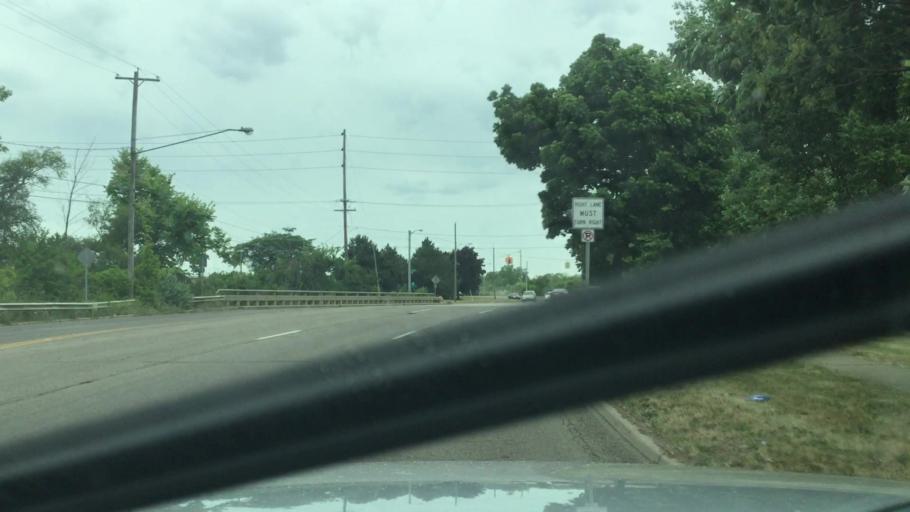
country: US
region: Michigan
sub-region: Genesee County
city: Flint
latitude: 43.0343
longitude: -83.6818
